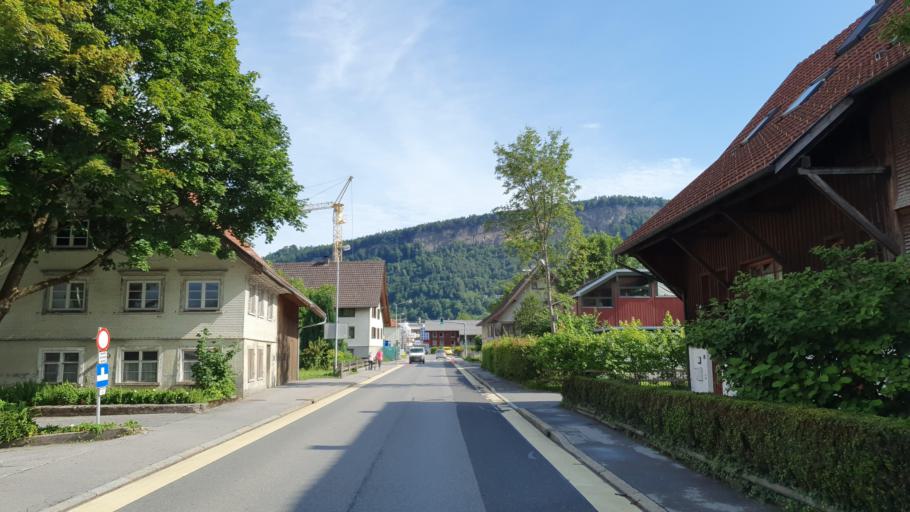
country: AT
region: Vorarlberg
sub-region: Politischer Bezirk Bregenz
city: Wolfurt
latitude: 47.4747
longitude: 9.7505
